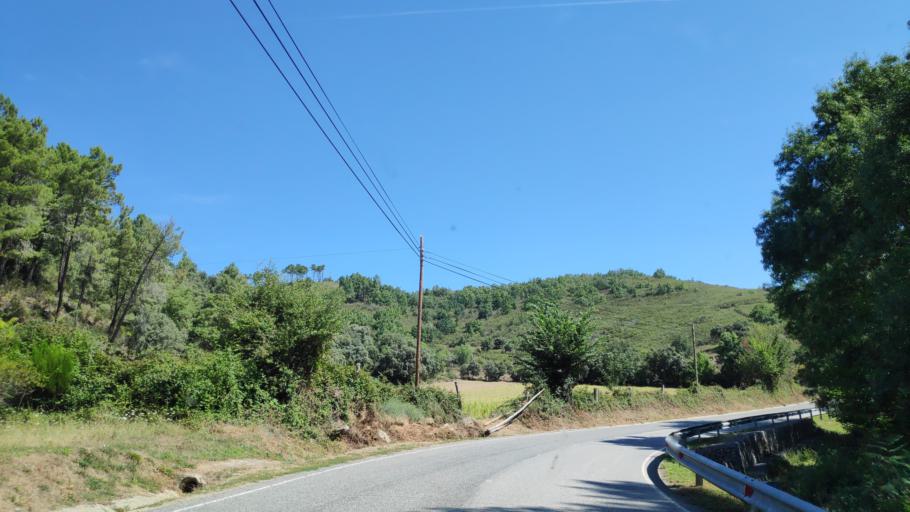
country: PT
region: Braganca
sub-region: Braganca Municipality
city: Braganca
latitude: 41.8875
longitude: -6.7356
